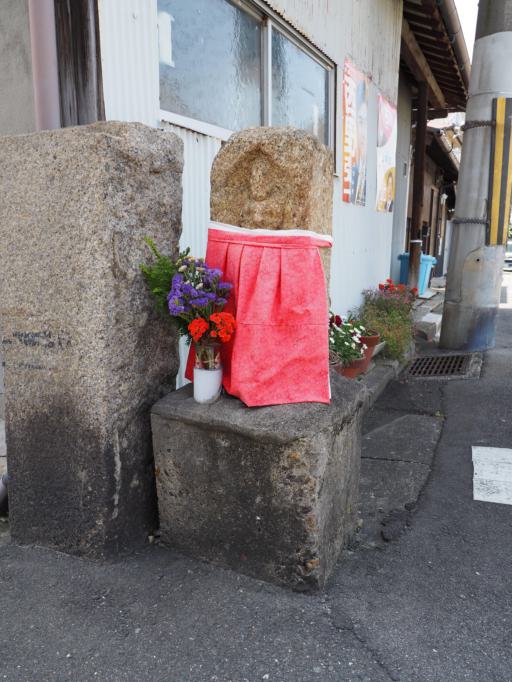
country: JP
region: Osaka
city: Daitocho
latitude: 34.6713
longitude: 135.5866
